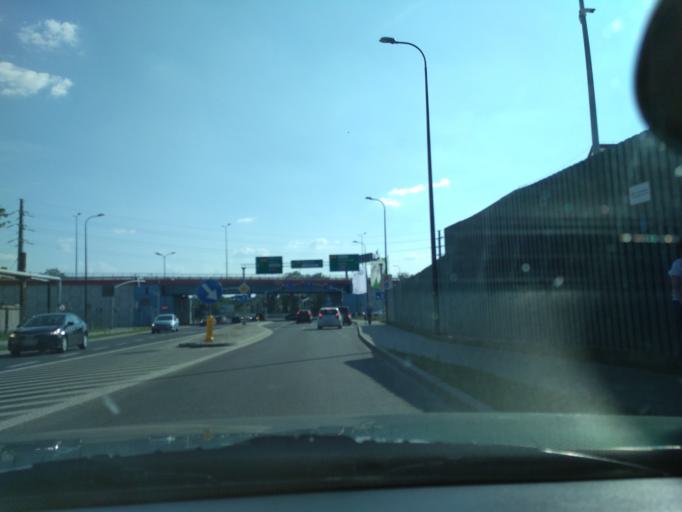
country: PL
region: Silesian Voivodeship
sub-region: Gliwice
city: Gliwice
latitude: 50.3054
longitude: 18.6611
